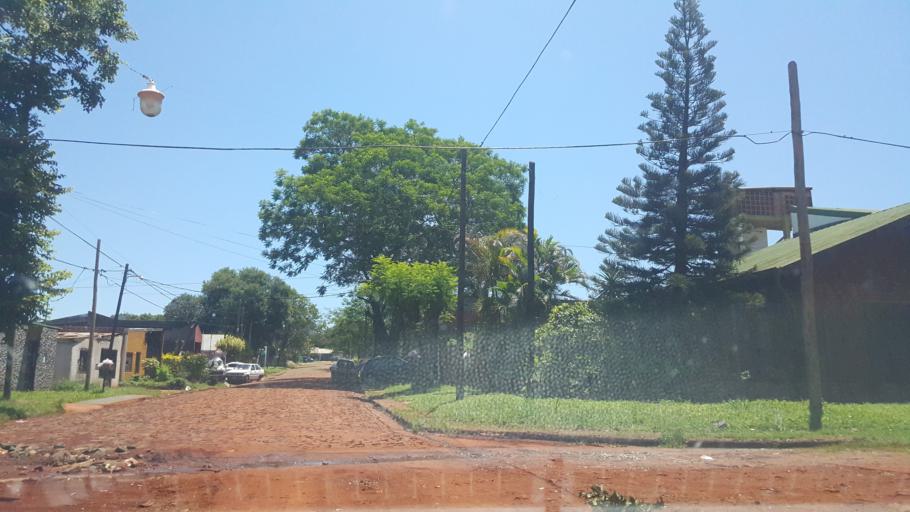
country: AR
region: Misiones
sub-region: Departamento de Capital
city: Posadas
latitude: -27.3992
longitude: -55.9114
